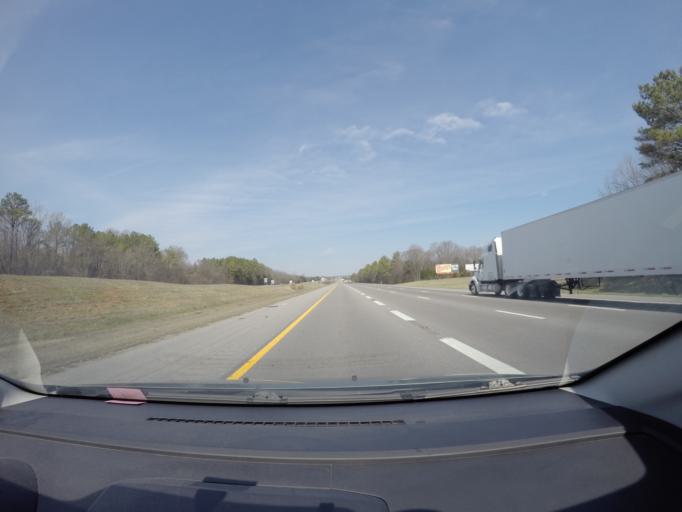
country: US
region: Tennessee
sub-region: Rutherford County
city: Smyrna
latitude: 35.9283
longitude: -86.5246
